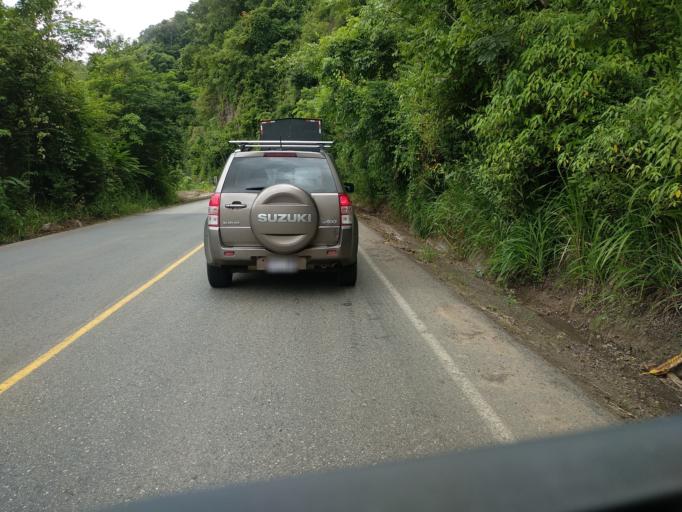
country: CR
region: Puntarenas
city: Buenos Aires
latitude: 9.0792
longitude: -83.2819
